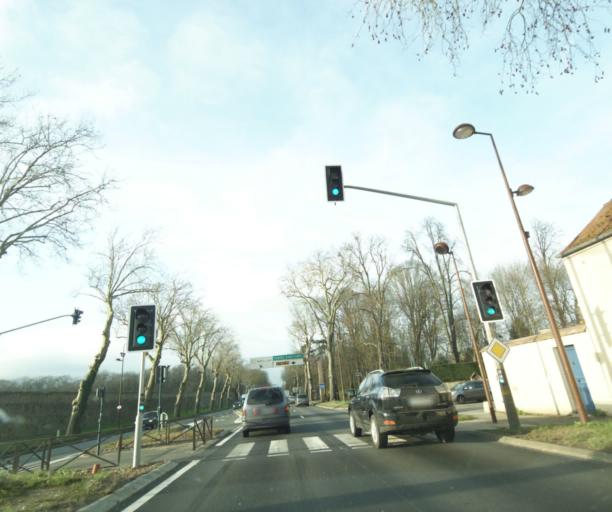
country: FR
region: Ile-de-France
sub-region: Departement des Yvelines
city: Louveciennes
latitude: 48.8553
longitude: 2.1074
